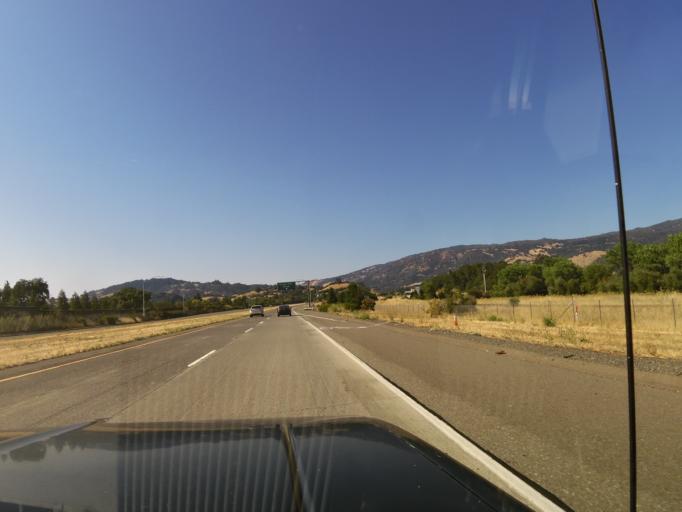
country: US
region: California
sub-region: Sonoma County
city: Cloverdale
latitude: 38.7950
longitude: -123.0121
